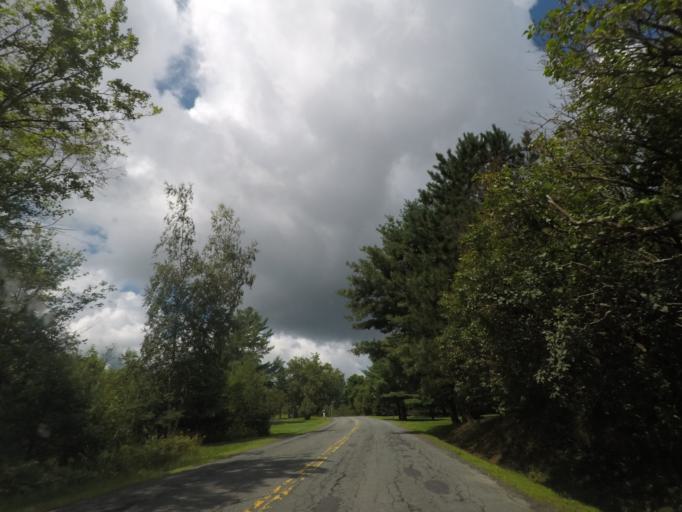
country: US
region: New York
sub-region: Rensselaer County
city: Averill Park
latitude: 42.6362
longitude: -73.4466
